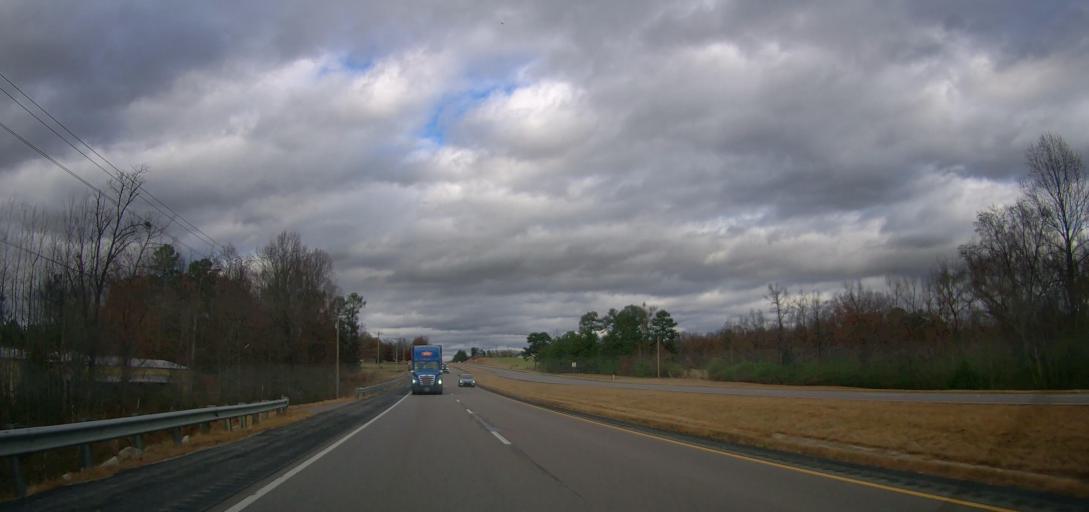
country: US
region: Alabama
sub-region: Morgan County
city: Falkville
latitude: 34.2953
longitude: -86.9983
